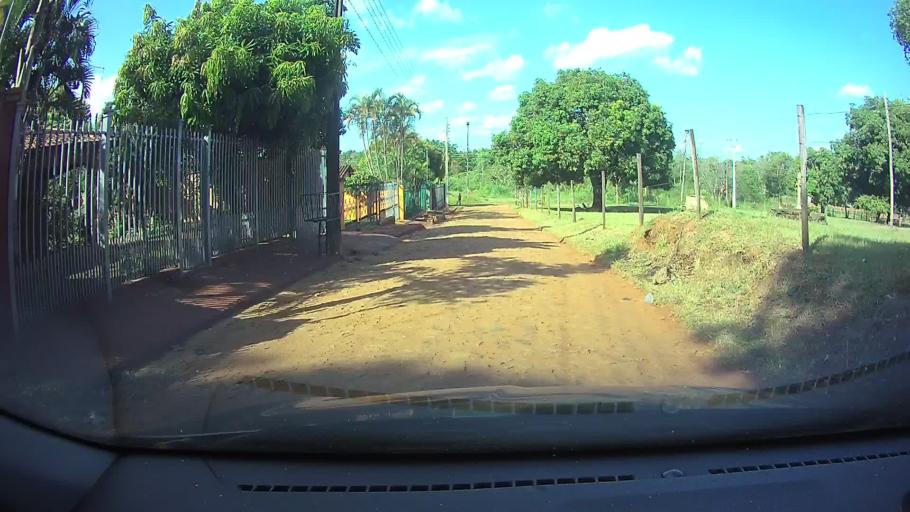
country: PY
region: Central
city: Limpio
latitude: -25.2397
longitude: -57.4639
